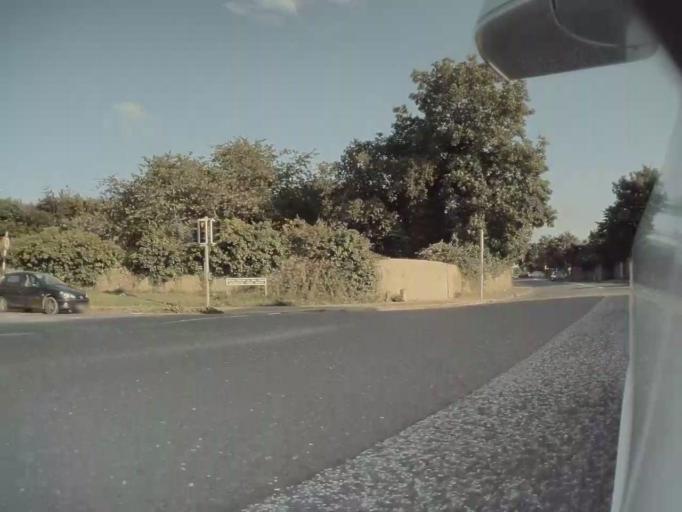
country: IE
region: Leinster
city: Foxrock
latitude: 53.2395
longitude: -6.1964
